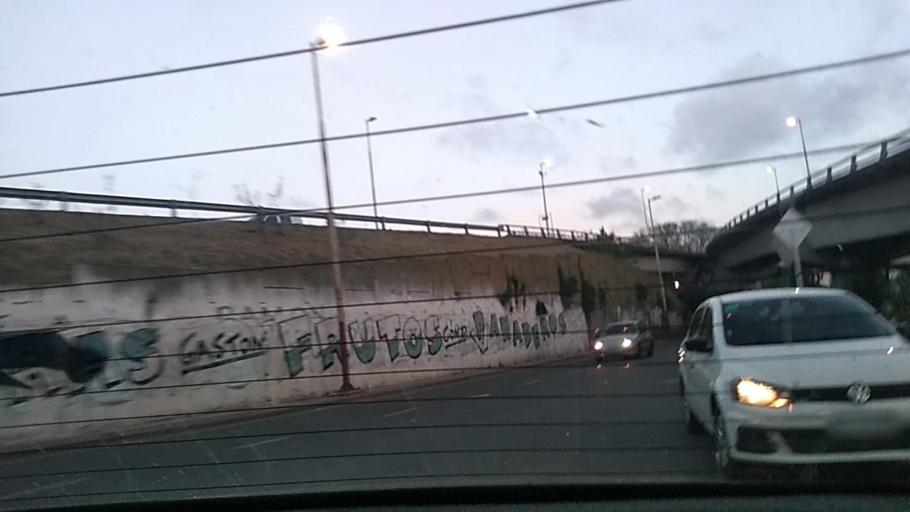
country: AR
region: Buenos Aires F.D.
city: Colegiales
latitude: -34.5475
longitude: -58.4381
